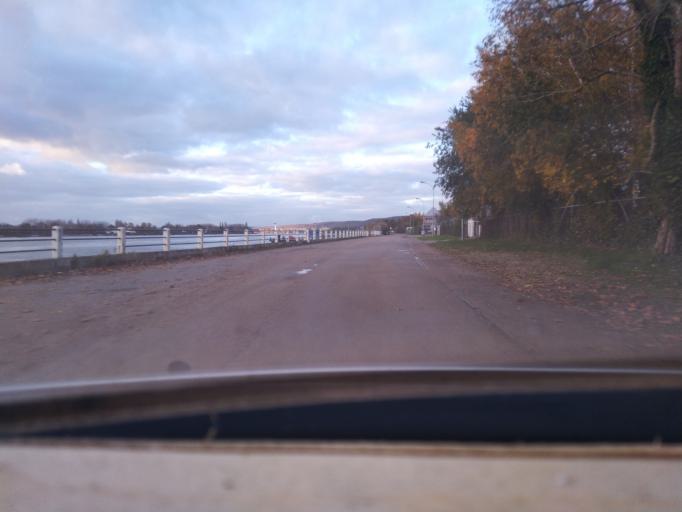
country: FR
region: Haute-Normandie
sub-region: Departement de la Seine-Maritime
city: Le Trait
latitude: 49.4597
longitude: 0.8188
